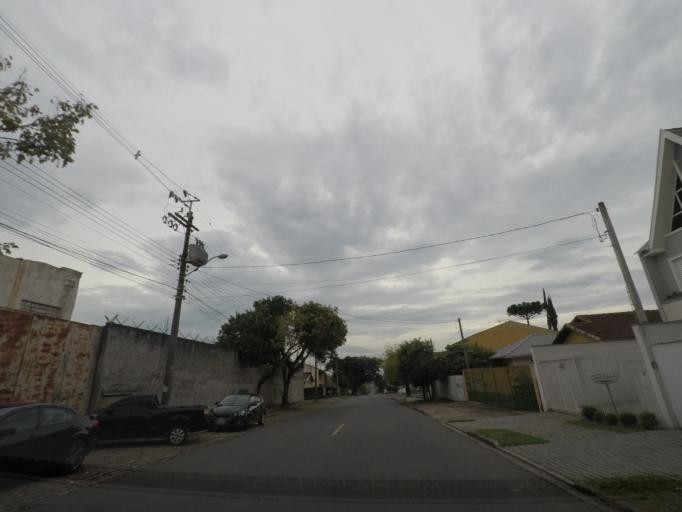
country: BR
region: Parana
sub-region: Curitiba
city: Curitiba
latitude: -25.4717
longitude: -49.3020
